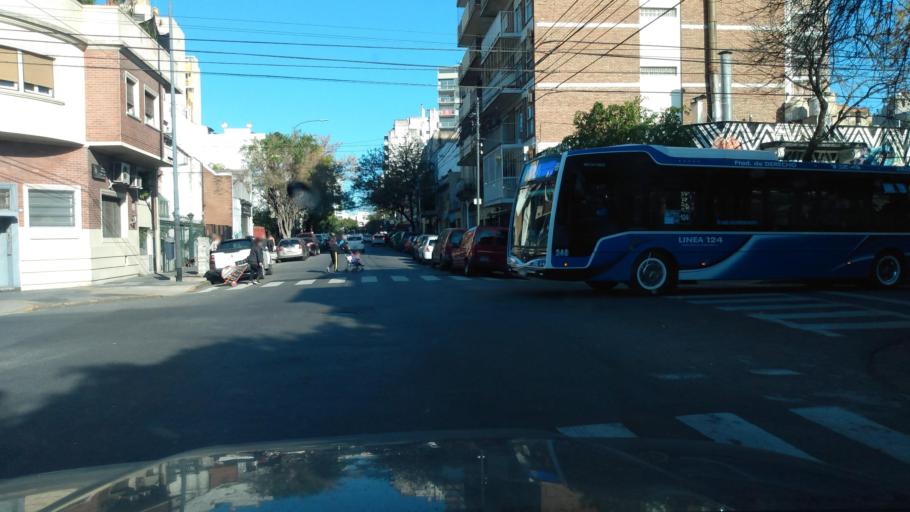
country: AR
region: Buenos Aires F.D.
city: Colegiales
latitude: -34.6044
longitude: -58.4401
